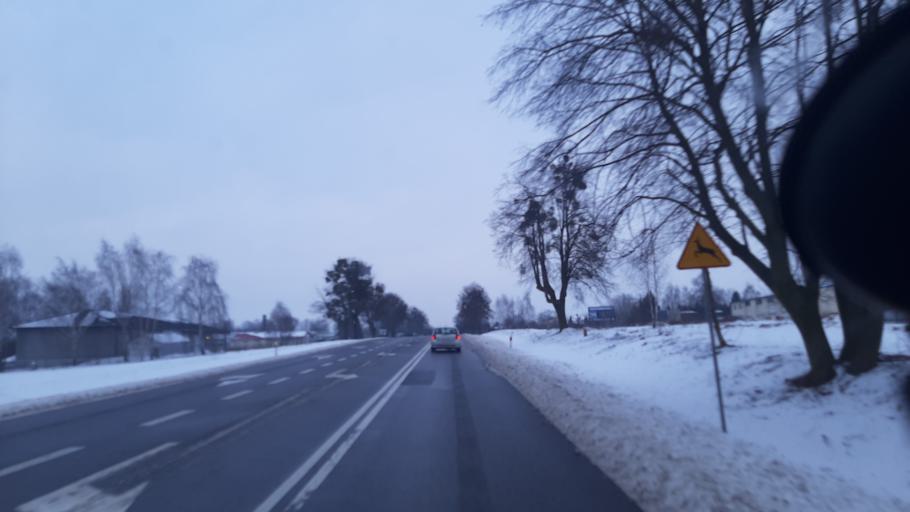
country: PL
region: Lublin Voivodeship
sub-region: Powiat lubelski
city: Garbow
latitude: 51.3594
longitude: 22.3145
